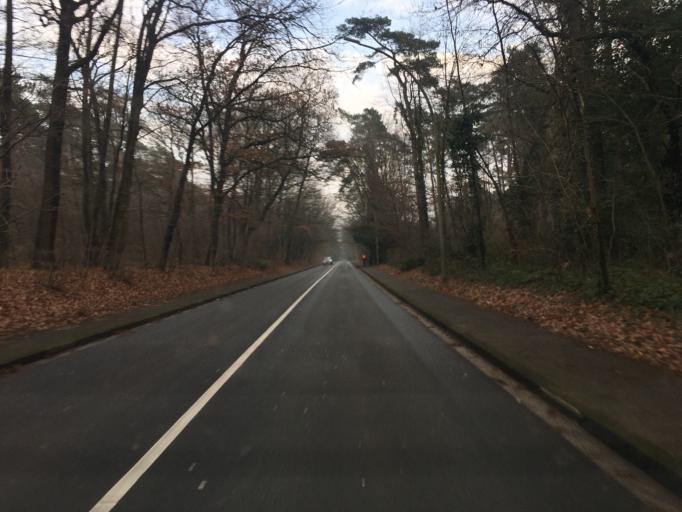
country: DE
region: North Rhine-Westphalia
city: Opladen
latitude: 51.0227
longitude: 7.0626
